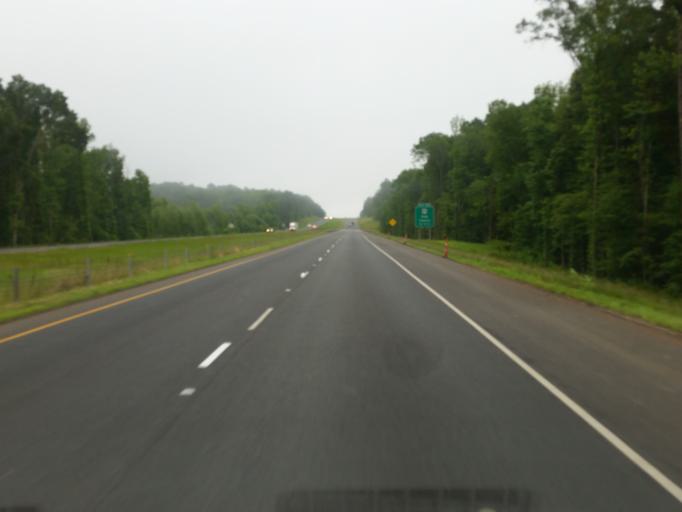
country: US
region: Louisiana
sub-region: Webster Parish
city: Minden
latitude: 32.5653
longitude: -93.1740
